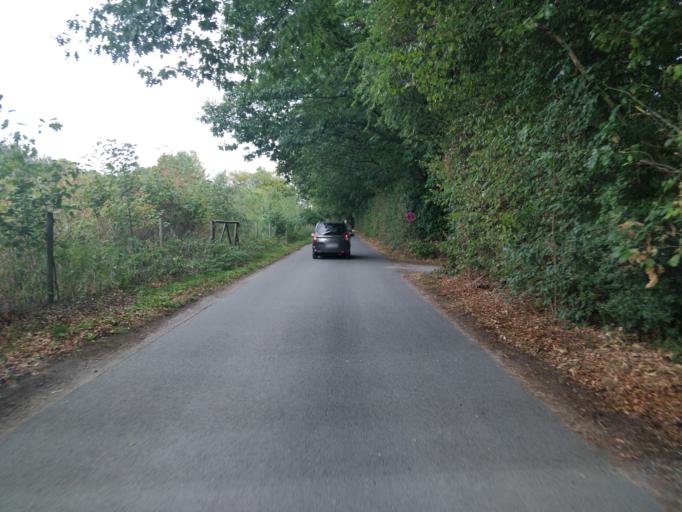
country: DE
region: North Rhine-Westphalia
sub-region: Regierungsbezirk Dusseldorf
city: Dormagen
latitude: 51.0825
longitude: 6.7878
